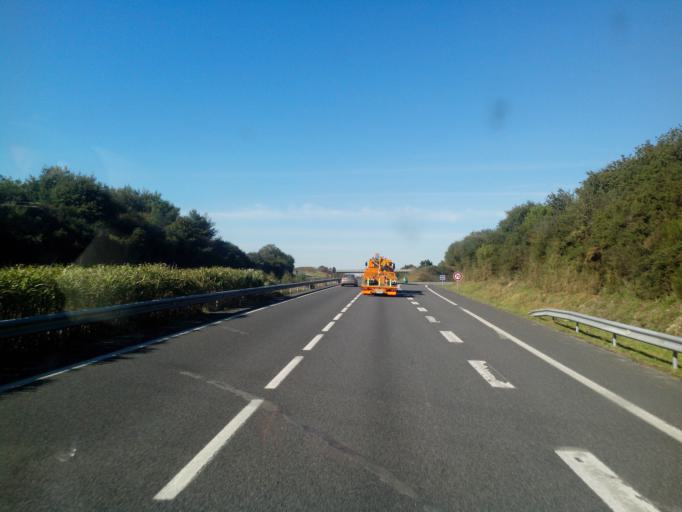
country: FR
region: Brittany
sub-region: Departement du Morbihan
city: Nivillac
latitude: 47.5179
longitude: -2.2789
